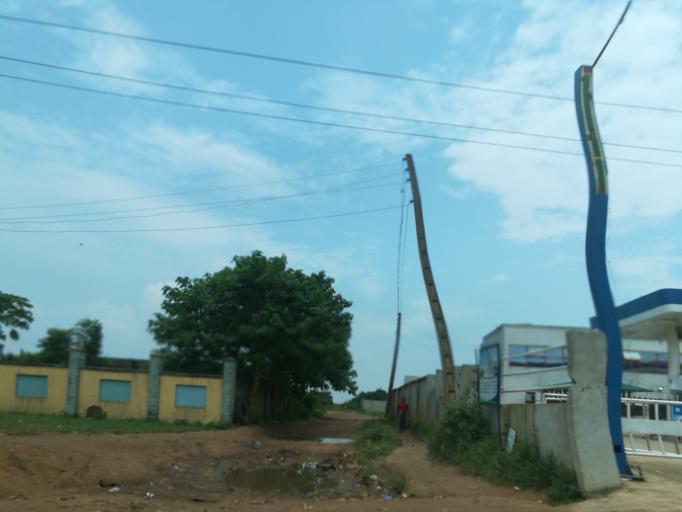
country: NG
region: Lagos
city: Ikorodu
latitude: 6.5826
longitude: 3.5881
